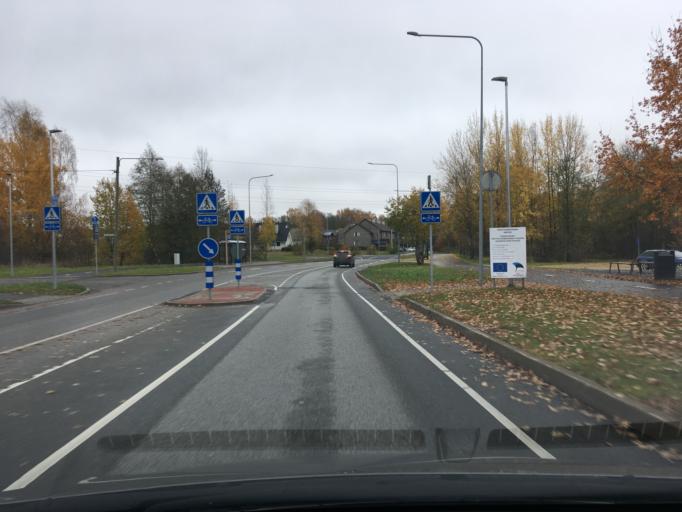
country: EE
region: Tartu
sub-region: Tartu linn
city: Tartu
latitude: 58.3600
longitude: 26.7772
